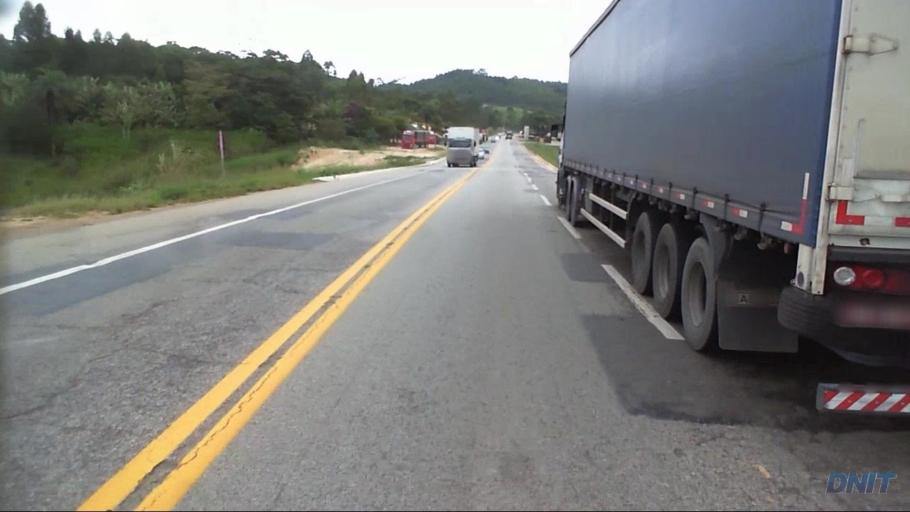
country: BR
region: Minas Gerais
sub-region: Caete
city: Caete
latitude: -19.7525
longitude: -43.5262
